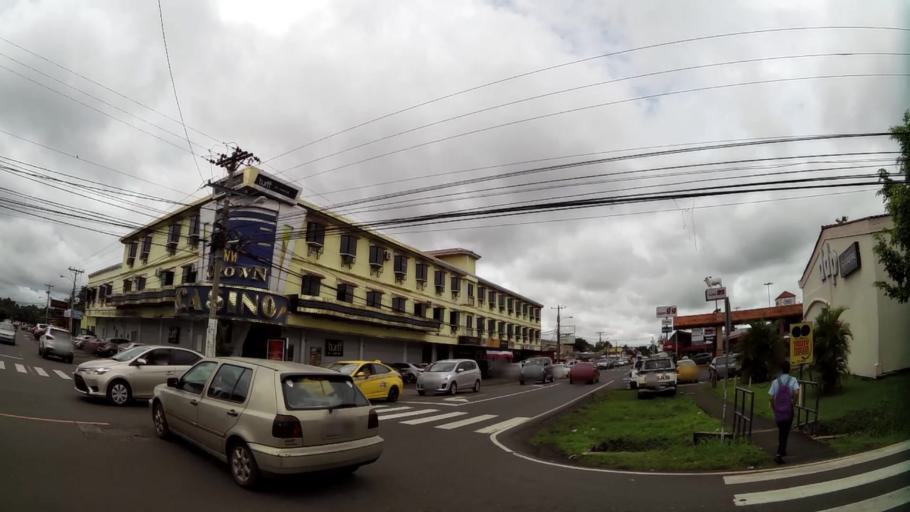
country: PA
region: Chiriqui
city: David
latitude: 8.4271
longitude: -82.4367
